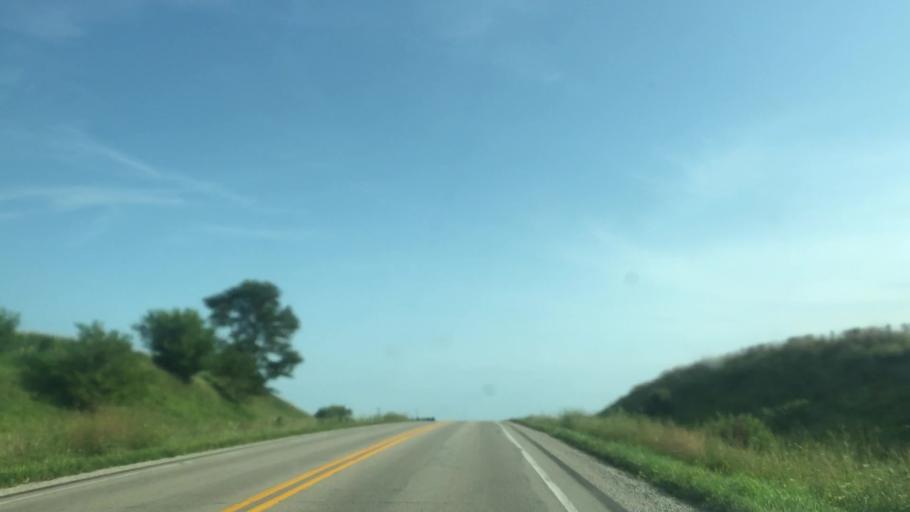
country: US
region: Iowa
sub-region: Marshall County
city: Marshalltown
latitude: 42.0436
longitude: -93.0002
